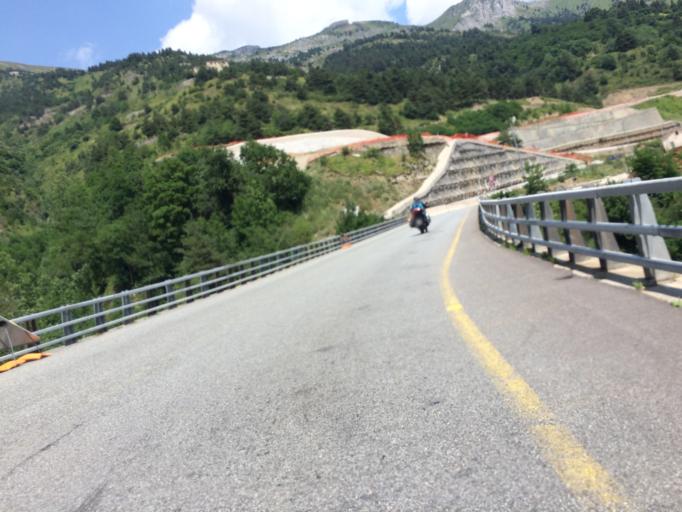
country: FR
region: Provence-Alpes-Cote d'Azur
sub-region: Departement des Alpes-Maritimes
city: Tende
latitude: 44.1358
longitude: 7.5672
